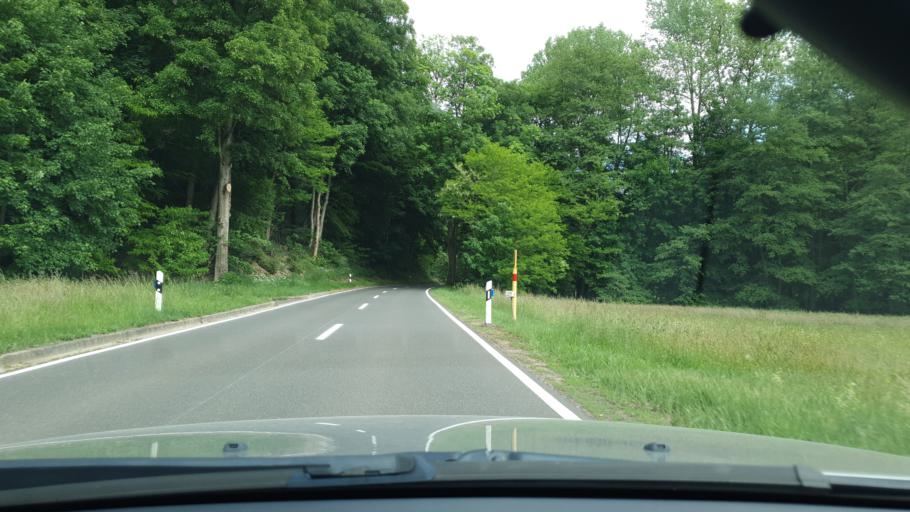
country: DE
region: Rheinland-Pfalz
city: Battweiler
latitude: 49.2788
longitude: 7.4446
